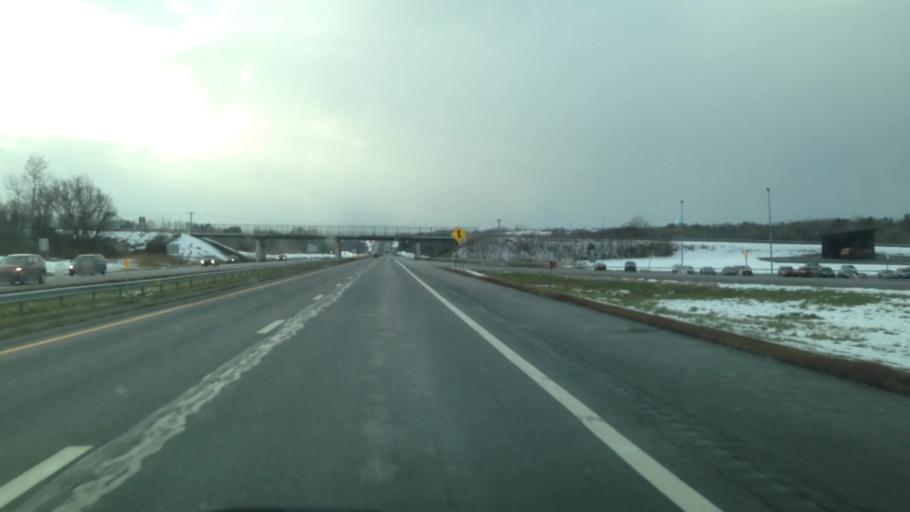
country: US
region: New York
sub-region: Montgomery County
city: Amsterdam
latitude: 42.9236
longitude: -74.1989
